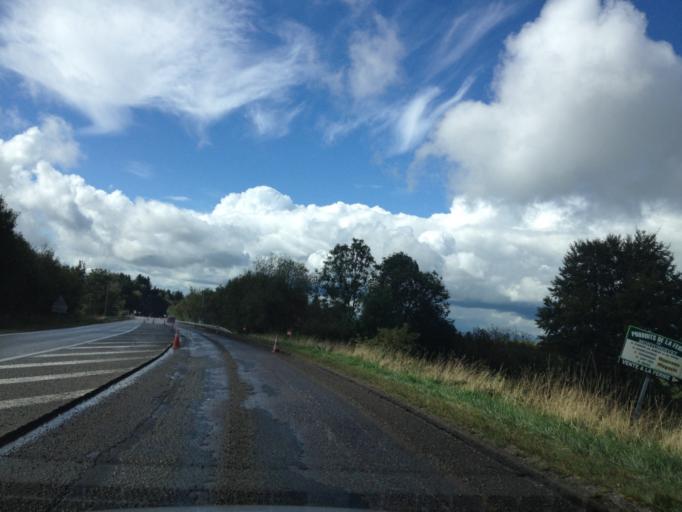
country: FR
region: Rhone-Alpes
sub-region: Departement du Rhone
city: Amplepuis
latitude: 45.9182
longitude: 4.3313
